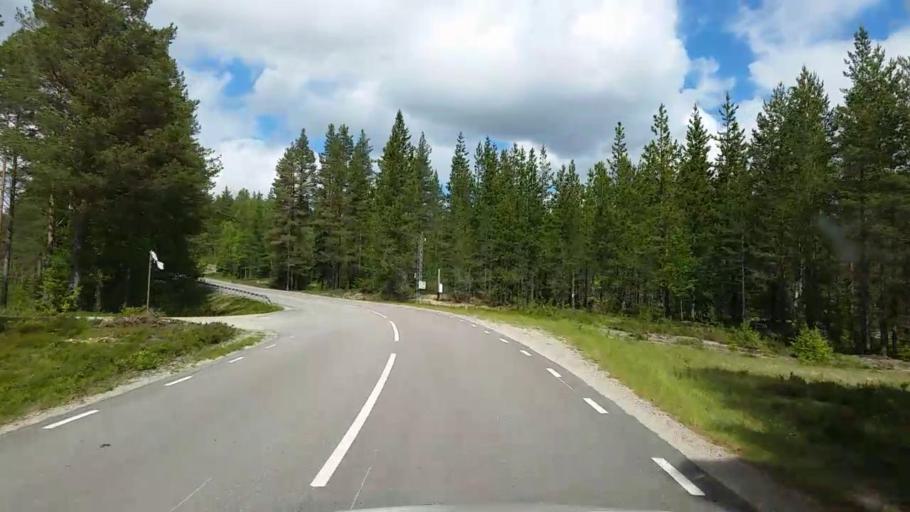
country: SE
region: Gaevleborg
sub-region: Bollnas Kommun
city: Vittsjo
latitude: 61.1316
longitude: 16.1766
